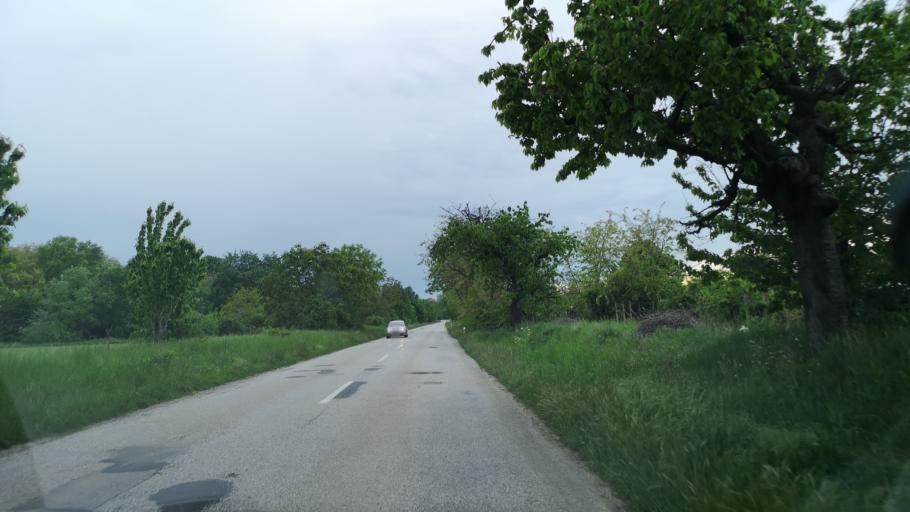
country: SK
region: Nitriansky
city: Sellye
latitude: 48.2568
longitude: 17.8796
